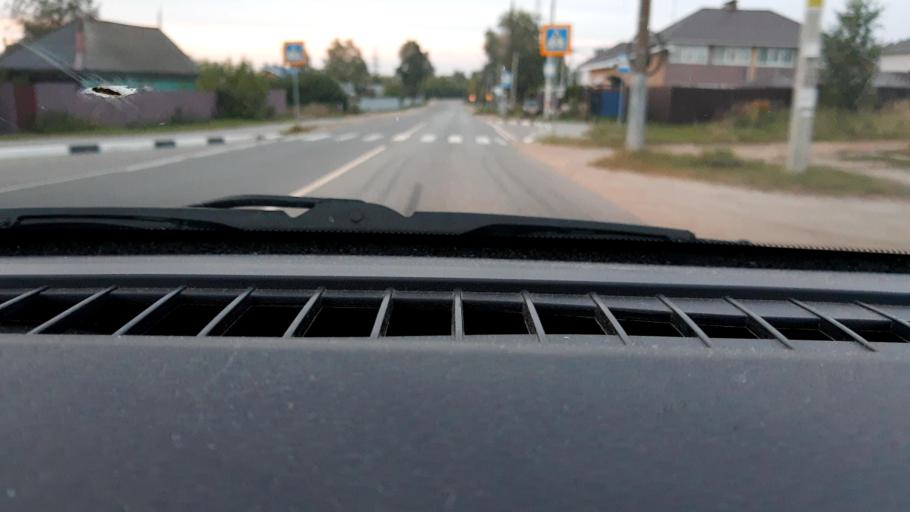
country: RU
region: Nizjnij Novgorod
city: Kstovo
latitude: 56.1700
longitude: 44.1759
